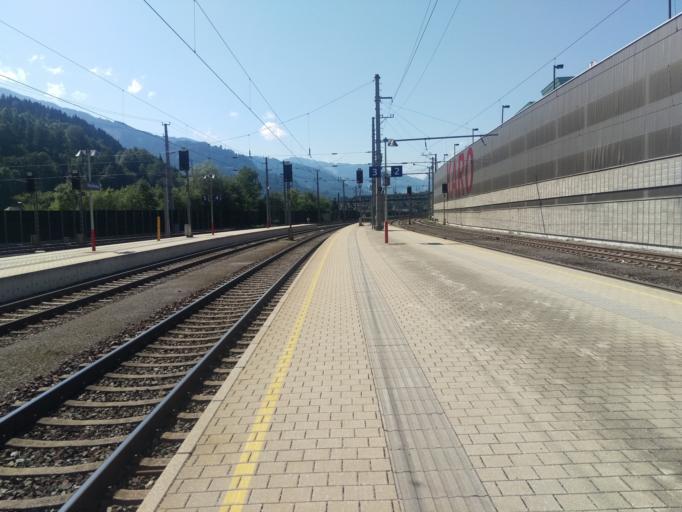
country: AT
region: Salzburg
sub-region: Politischer Bezirk Sankt Johann im Pongau
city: Bischofshofen
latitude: 47.4174
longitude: 13.2201
